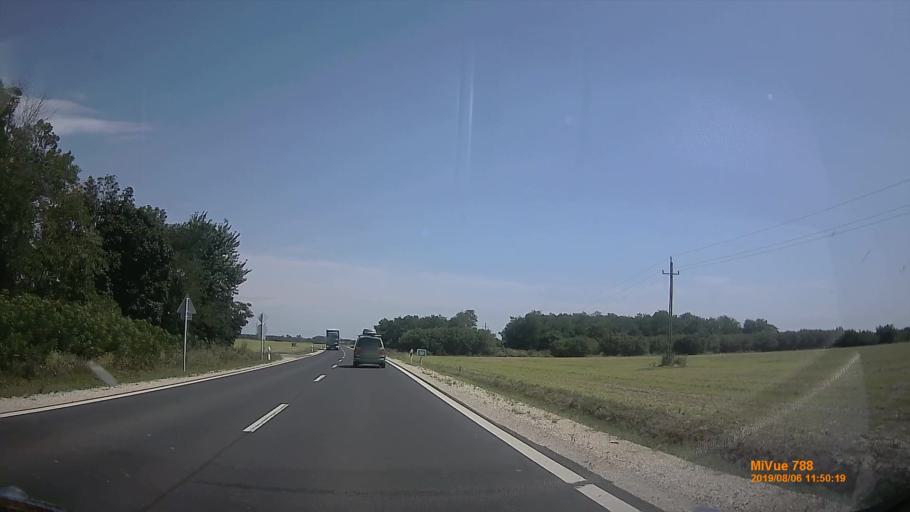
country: HU
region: Vas
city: Kormend
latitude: 47.0239
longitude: 16.6245
